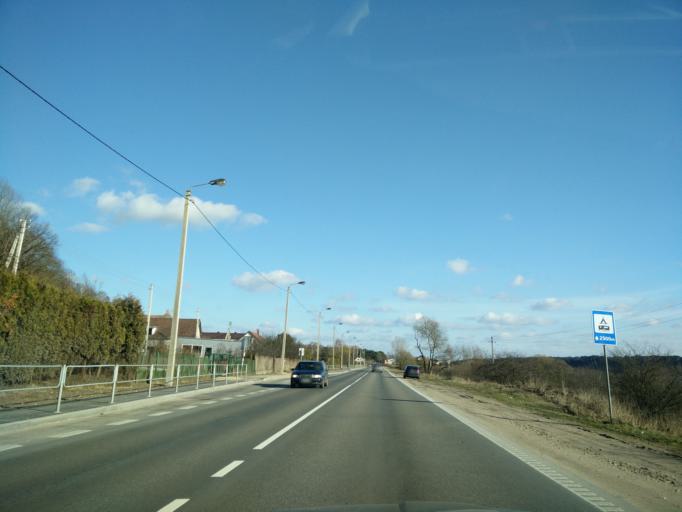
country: LT
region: Kauno apskritis
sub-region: Kauno rajonas
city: Akademija (Kaunas)
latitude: 54.9221
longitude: 23.7965
